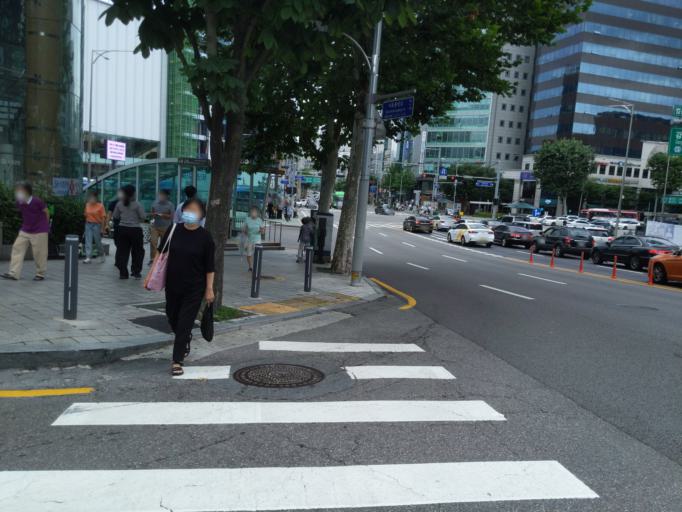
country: KR
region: Seoul
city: Seoul
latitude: 37.4944
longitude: 127.0135
